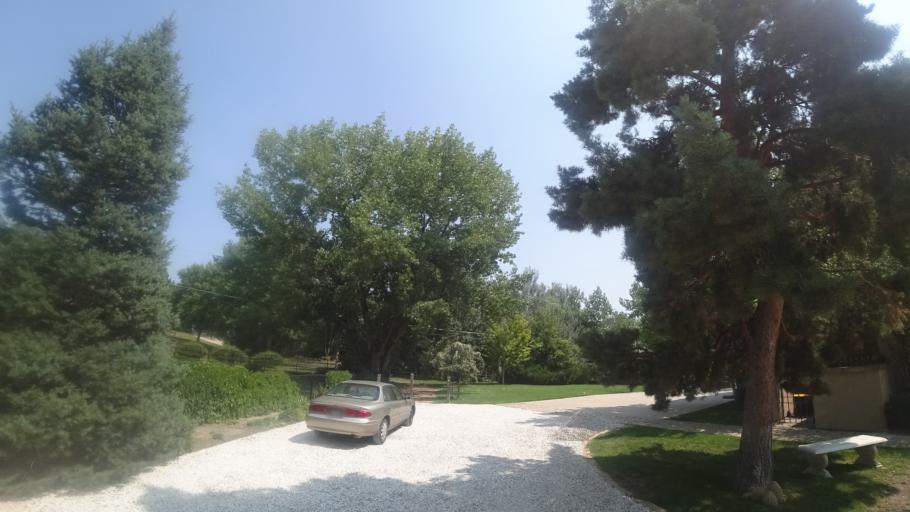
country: US
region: Colorado
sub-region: Arapahoe County
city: Cherry Hills Village
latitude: 39.6359
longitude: -104.9647
